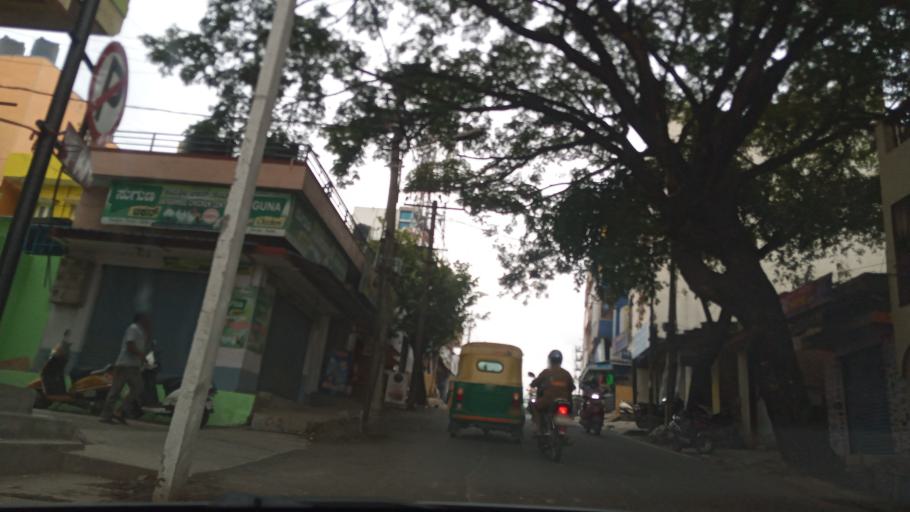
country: IN
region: Karnataka
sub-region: Bangalore Urban
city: Bangalore
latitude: 13.0087
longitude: 77.5411
